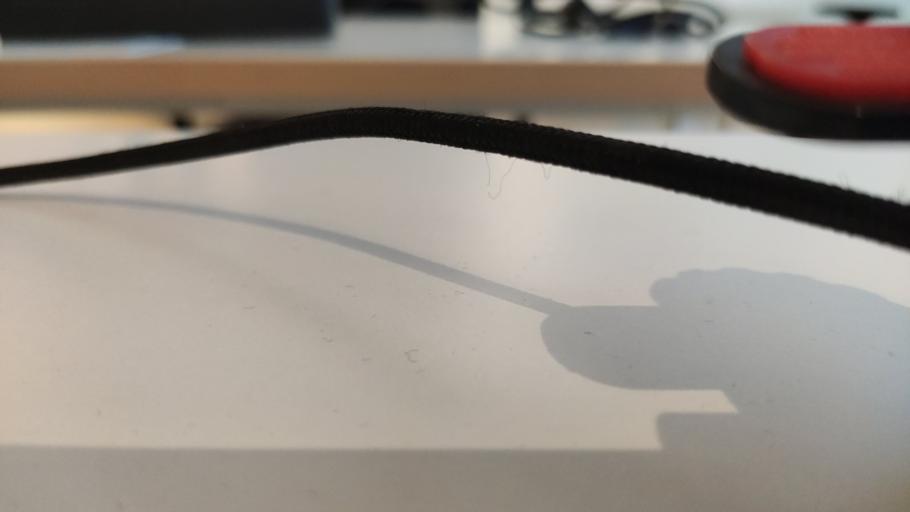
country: RU
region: Moskovskaya
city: Novopetrovskoye
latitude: 55.9021
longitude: 36.4378
